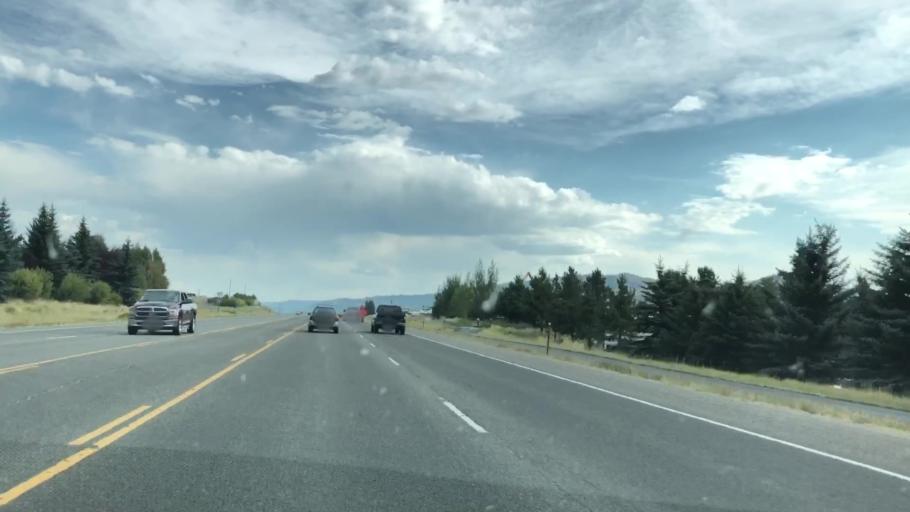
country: US
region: Wyoming
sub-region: Teton County
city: South Park
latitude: 43.4232
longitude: -110.7769
